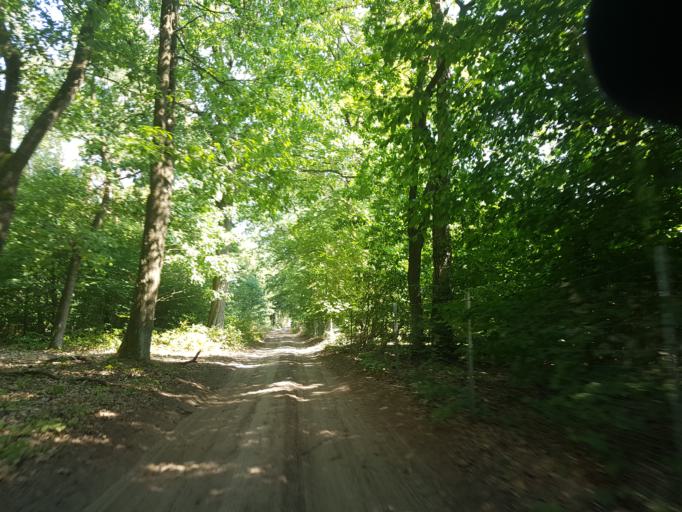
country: DE
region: Brandenburg
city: Gorzke
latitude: 52.0722
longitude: 12.3682
